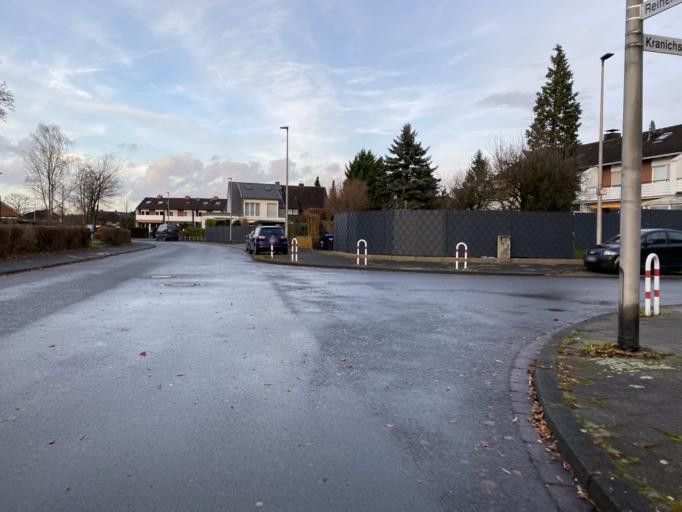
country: DE
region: North Rhine-Westphalia
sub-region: Regierungsbezirk Arnsberg
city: Hamm
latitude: 51.6848
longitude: 7.8663
